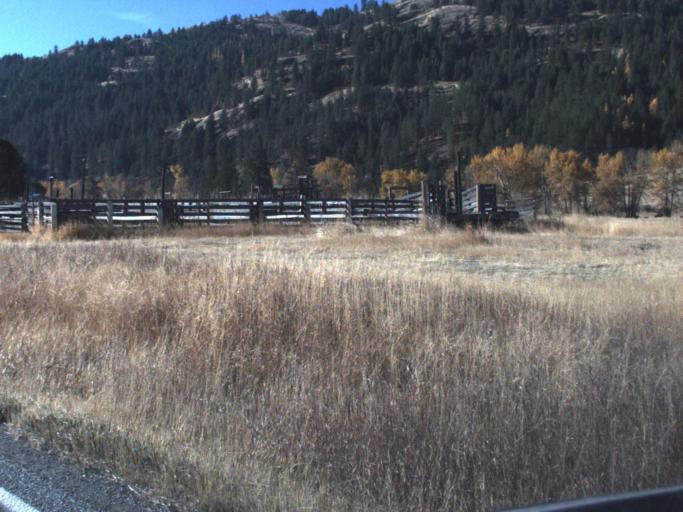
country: US
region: Washington
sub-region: Ferry County
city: Republic
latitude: 48.8215
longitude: -118.5945
